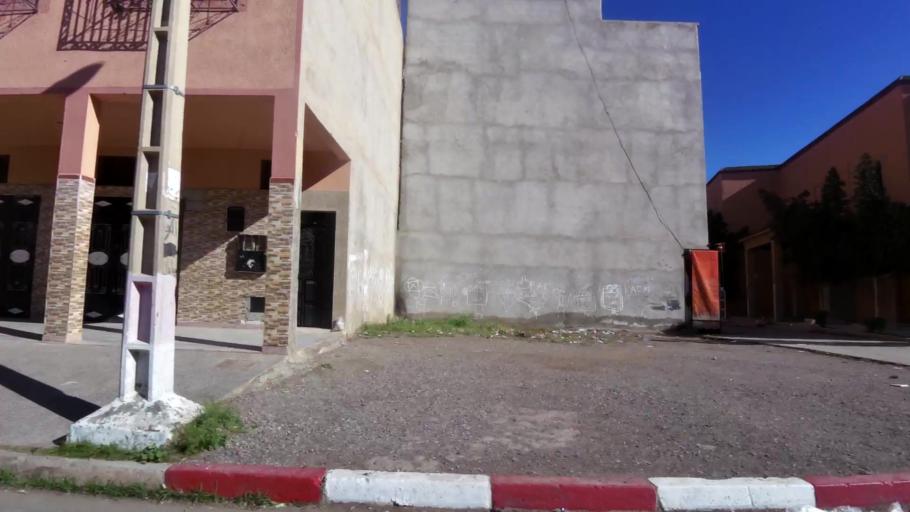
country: MA
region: Marrakech-Tensift-Al Haouz
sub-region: Marrakech
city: Marrakesh
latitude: 31.6007
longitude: -8.0341
